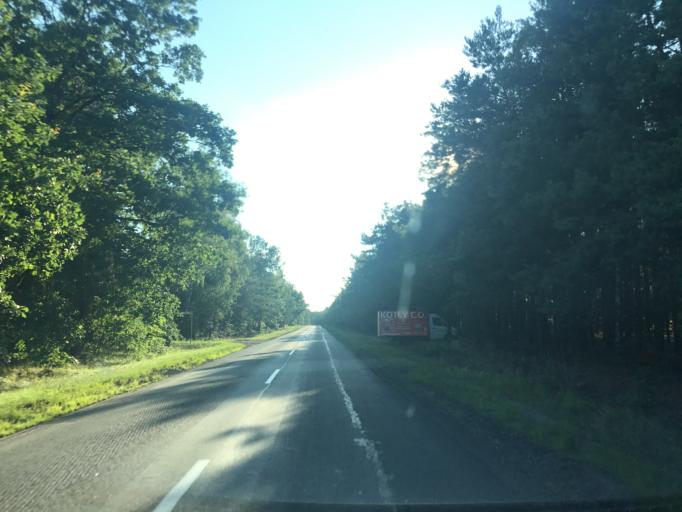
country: PL
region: Greater Poland Voivodeship
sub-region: Powiat pleszewski
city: Chocz
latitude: 52.0599
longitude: 17.8656
